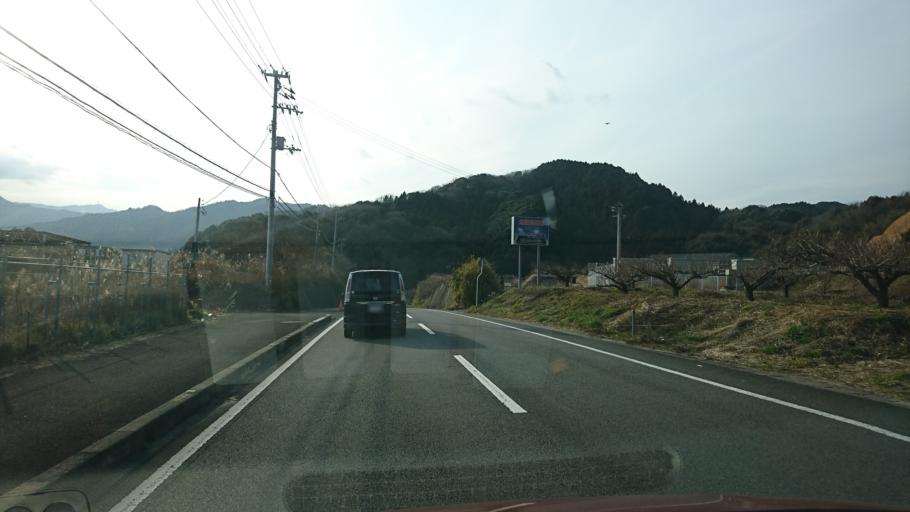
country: JP
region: Ehime
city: Hojo
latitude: 33.9966
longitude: 132.9233
